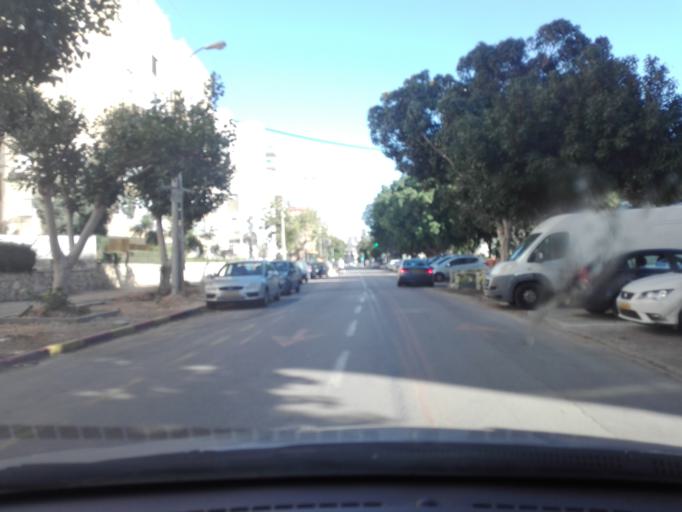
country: IL
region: Central District
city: Netanya
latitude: 32.3242
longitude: 34.8516
